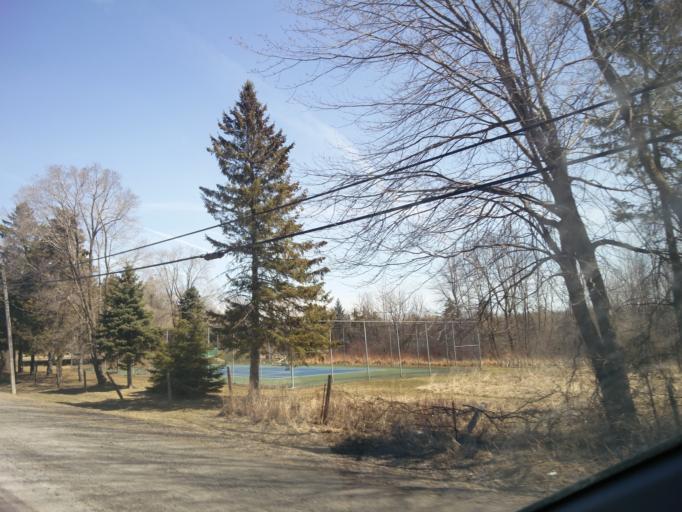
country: CA
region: Ontario
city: Bells Corners
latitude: 45.1806
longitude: -75.6385
